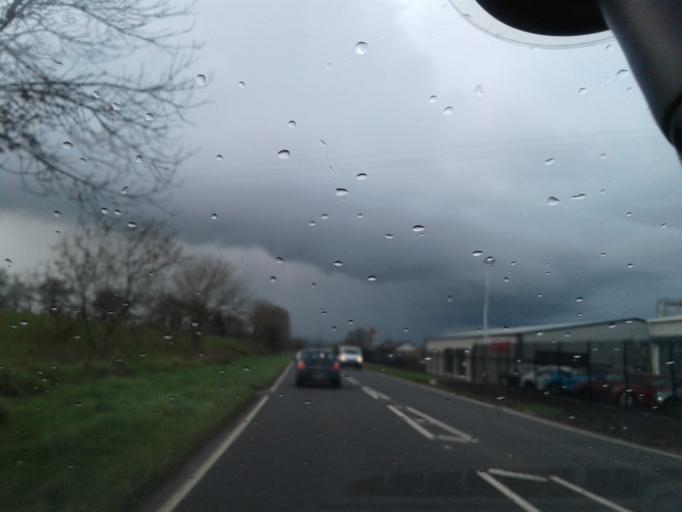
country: GB
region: Northern Ireland
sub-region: Strabane District
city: Sion Mills
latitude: 54.7563
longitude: -7.4512
